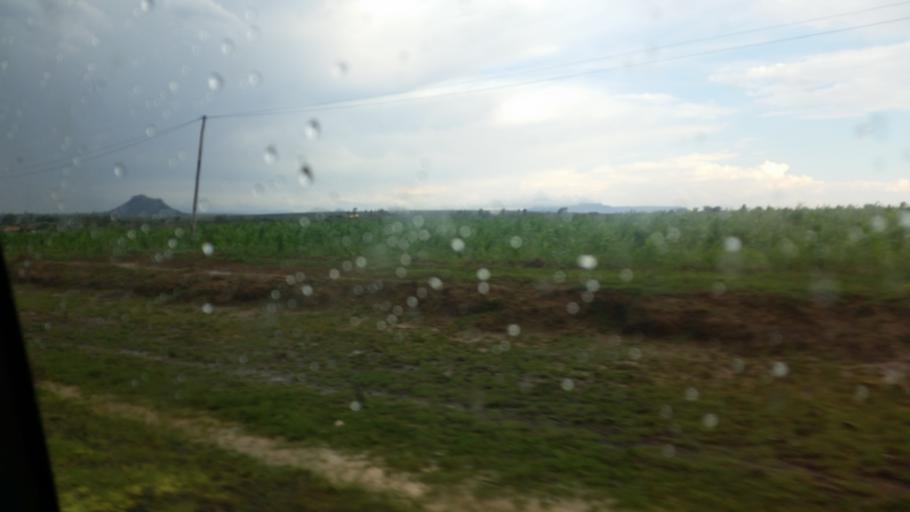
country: LS
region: Mafeteng
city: Mafeteng
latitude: -29.7560
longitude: 27.1214
